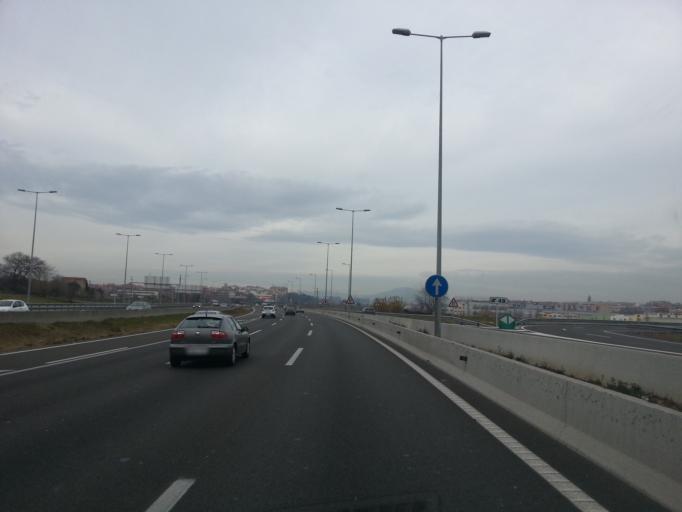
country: ES
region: Catalonia
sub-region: Provincia de Barcelona
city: Ripollet
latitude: 41.4882
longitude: 2.1590
